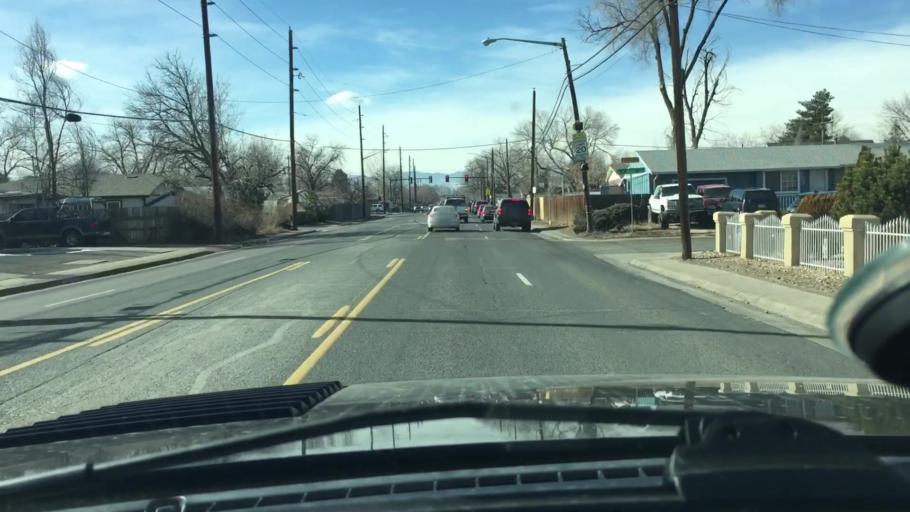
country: US
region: Colorado
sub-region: Adams County
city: Westminster
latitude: 39.8273
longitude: -105.0452
